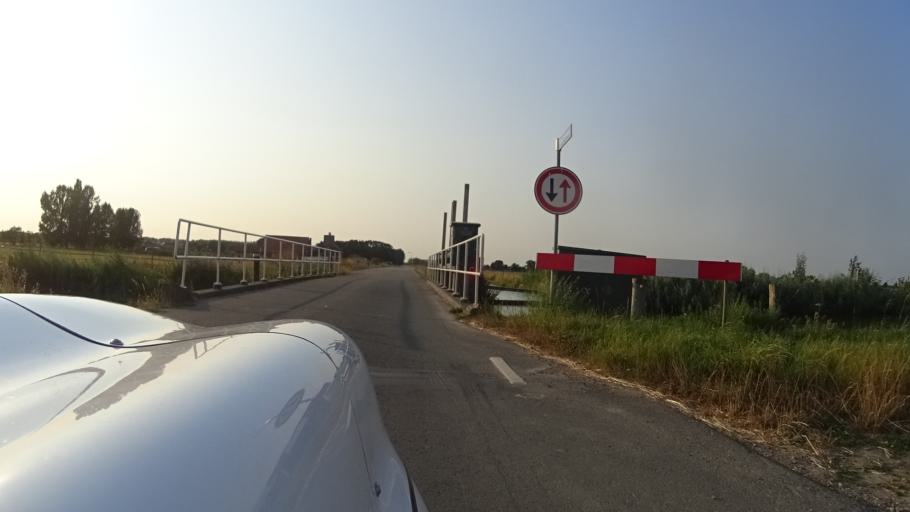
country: NL
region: North Brabant
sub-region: Gemeente Oss
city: Oss
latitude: 51.8531
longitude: 5.5218
